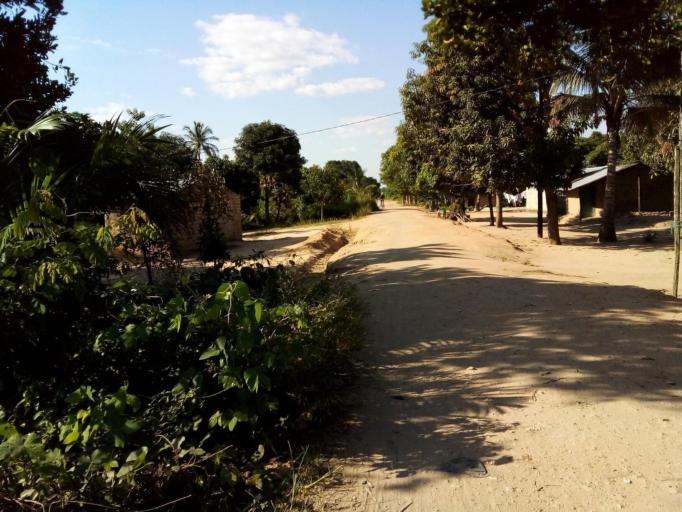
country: MZ
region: Zambezia
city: Quelimane
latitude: -17.5998
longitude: 36.8256
